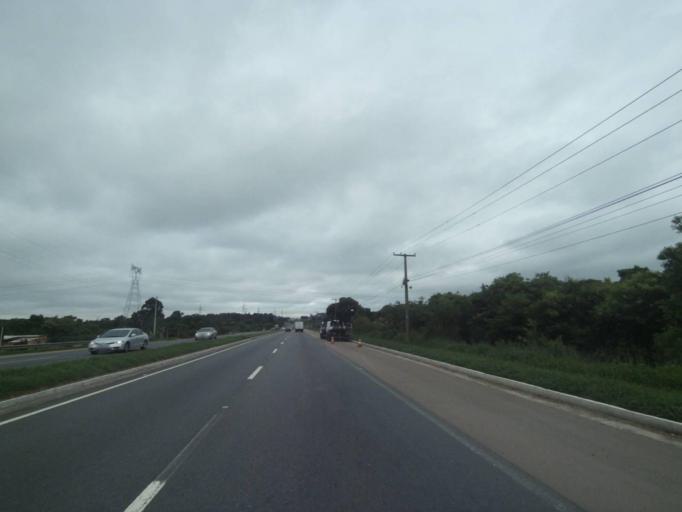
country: BR
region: Parana
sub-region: Araucaria
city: Araucaria
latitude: -25.5555
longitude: -49.3416
